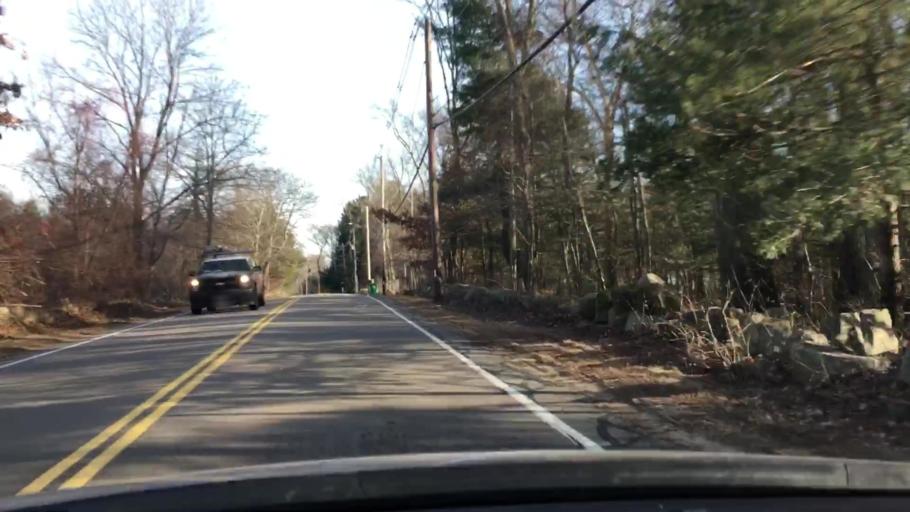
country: US
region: Massachusetts
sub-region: Norfolk County
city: Westwood
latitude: 42.2229
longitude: -71.2152
